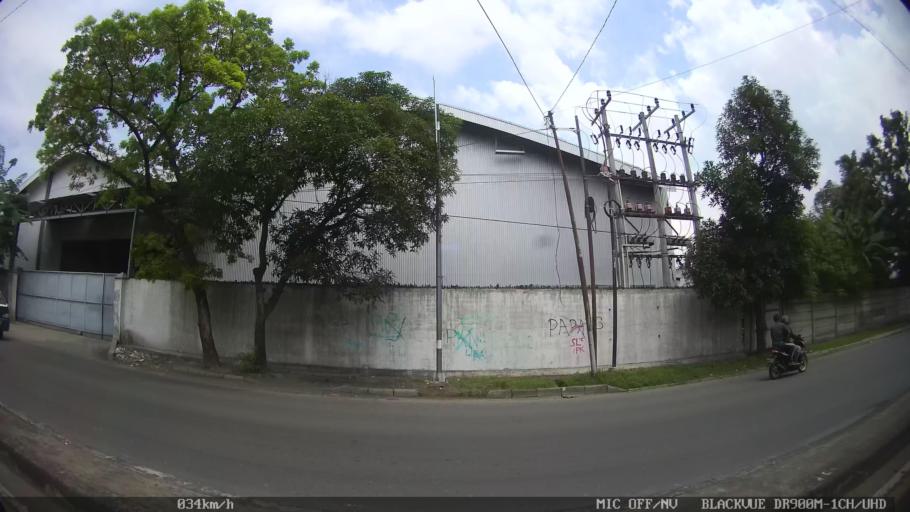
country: ID
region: North Sumatra
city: Labuhan Deli
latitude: 3.6566
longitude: 98.6647
